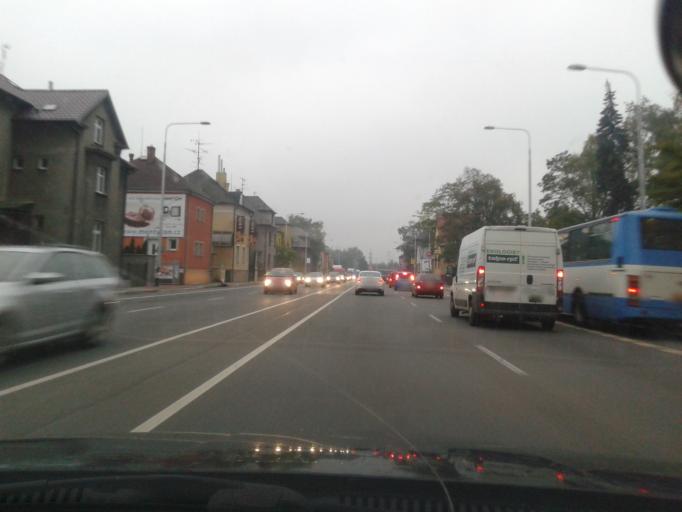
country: CZ
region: Moravskoslezsky
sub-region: Okres Ostrava-Mesto
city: Ostrava
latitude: 49.8004
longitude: 18.2536
